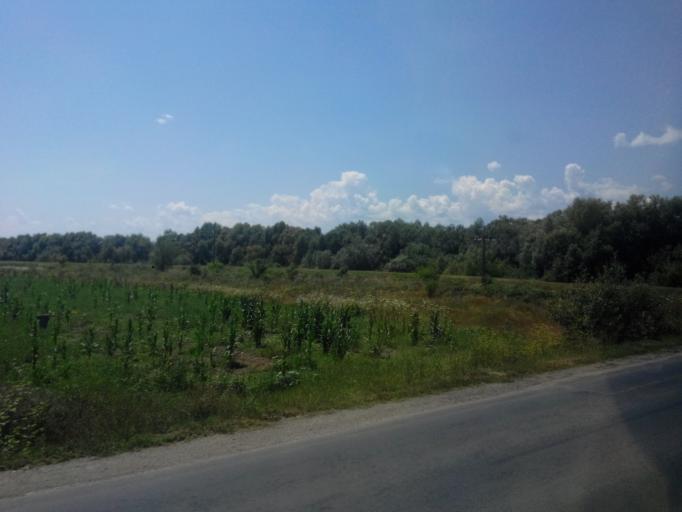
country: RO
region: Hunedoara
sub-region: Municipiul Deva
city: Cristur
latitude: 45.8553
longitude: 22.9578
